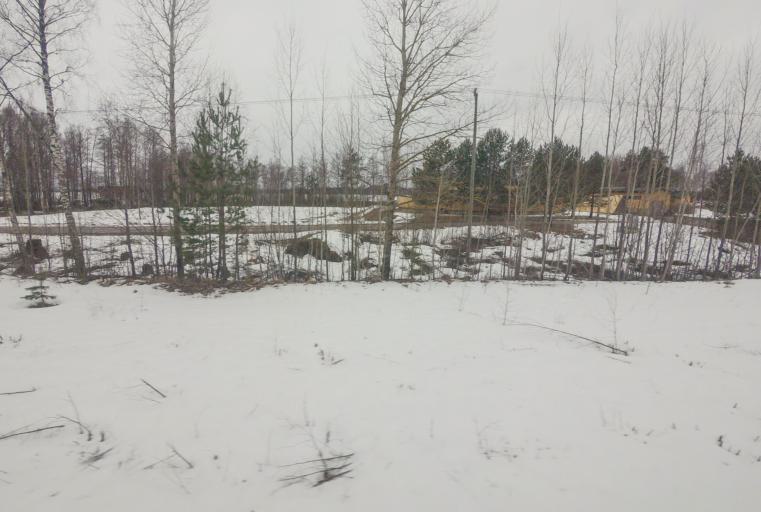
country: FI
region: South Karelia
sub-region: Imatra
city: Parikkala
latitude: 61.5942
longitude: 29.4849
